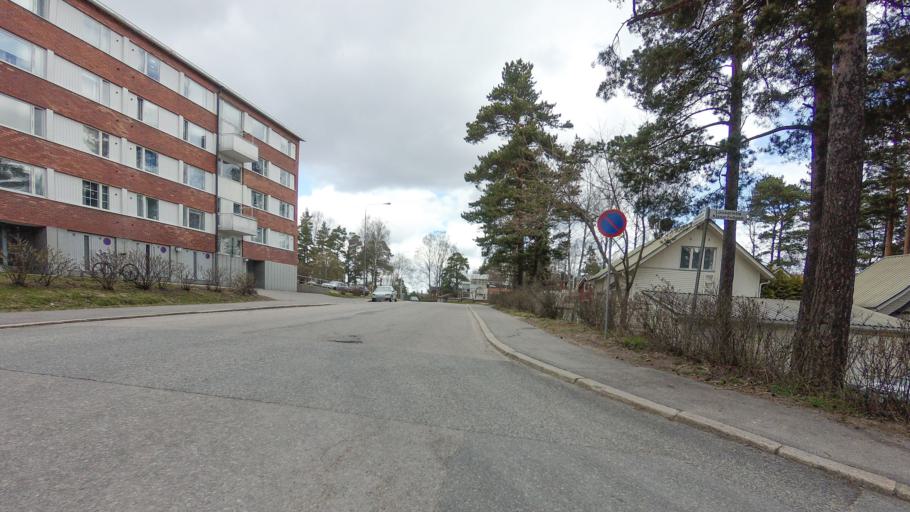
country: FI
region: Uusimaa
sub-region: Helsinki
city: Vantaa
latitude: 60.2159
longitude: 25.1052
